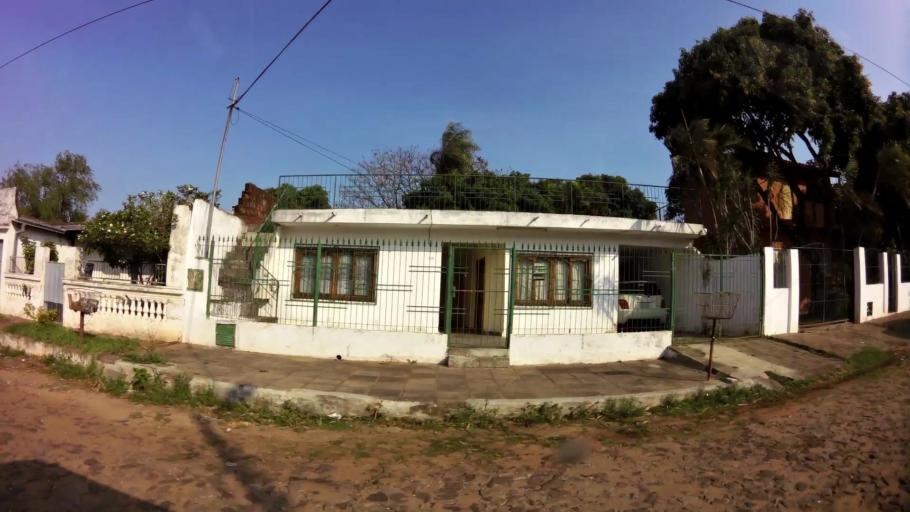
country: PY
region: Central
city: Lambare
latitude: -25.3467
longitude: -57.5861
